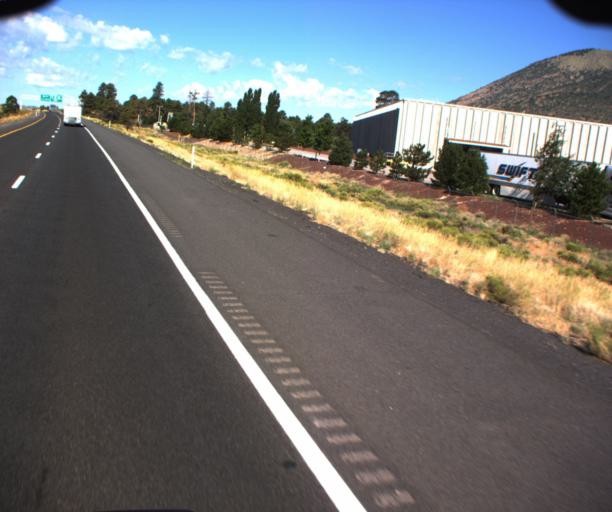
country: US
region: Arizona
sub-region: Coconino County
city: Flagstaff
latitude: 35.2185
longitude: -111.5740
